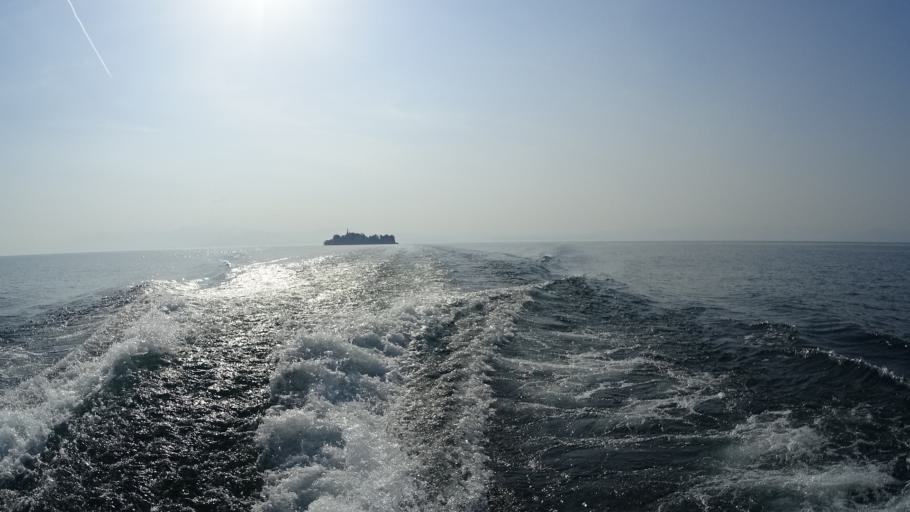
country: JP
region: Shiga Prefecture
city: Hikone
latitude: 35.2950
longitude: 136.1911
